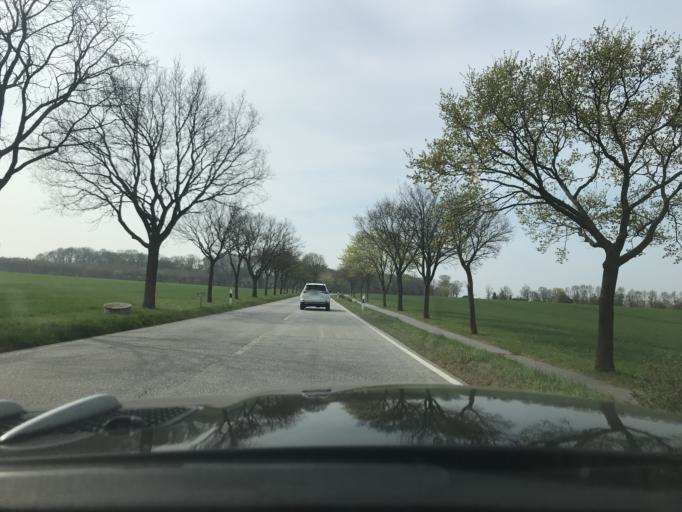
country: DE
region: Schleswig-Holstein
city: Grube
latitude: 54.2581
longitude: 11.0335
